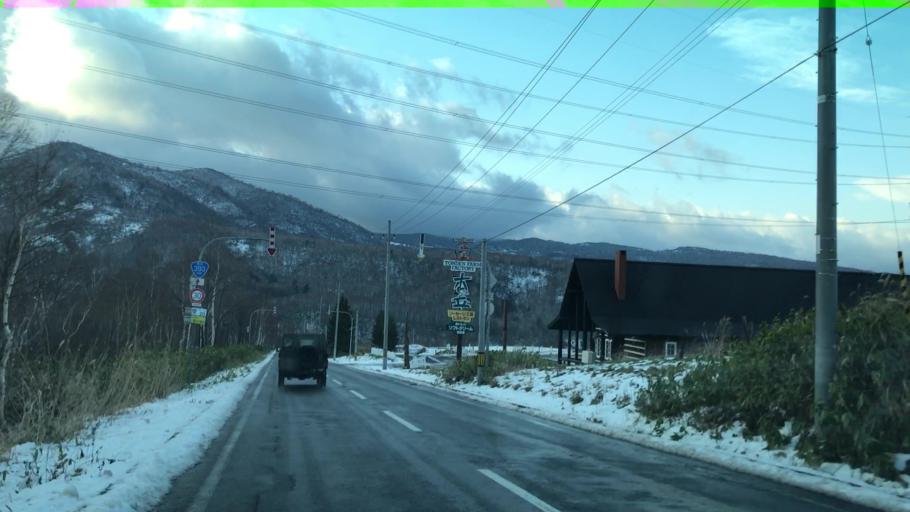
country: JP
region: Hokkaido
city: Otaru
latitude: 43.0912
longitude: 140.9748
